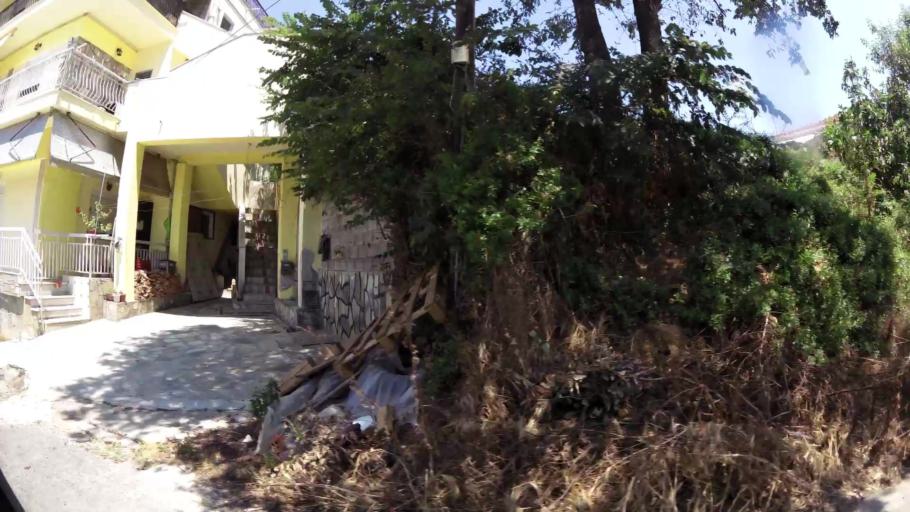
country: GR
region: Central Macedonia
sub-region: Nomos Thessalonikis
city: Epanomi
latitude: 40.4278
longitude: 22.9325
